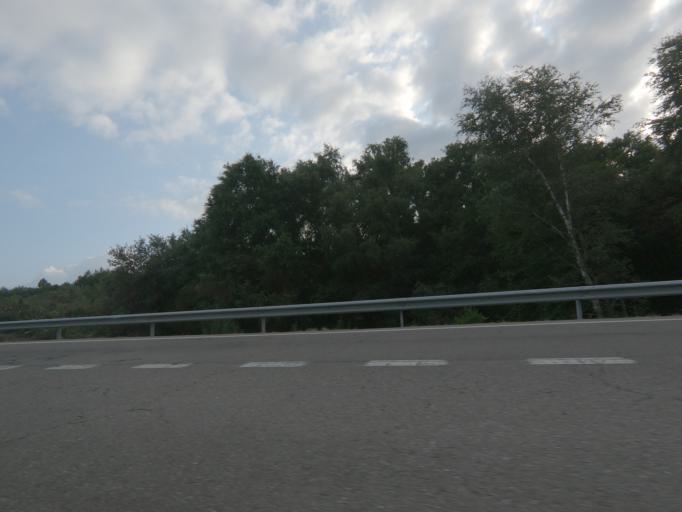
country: ES
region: Galicia
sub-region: Provincia de Ourense
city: Taboadela
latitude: 42.2224
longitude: -7.8427
